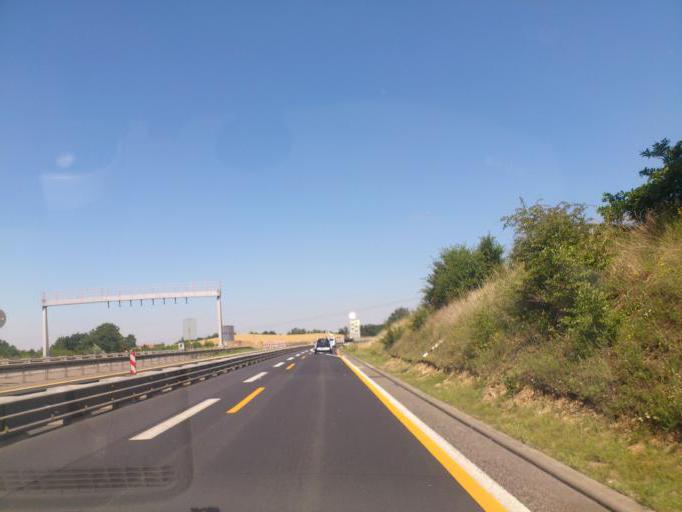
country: DE
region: Saxony
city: Albertstadt
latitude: 51.1425
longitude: 13.7482
